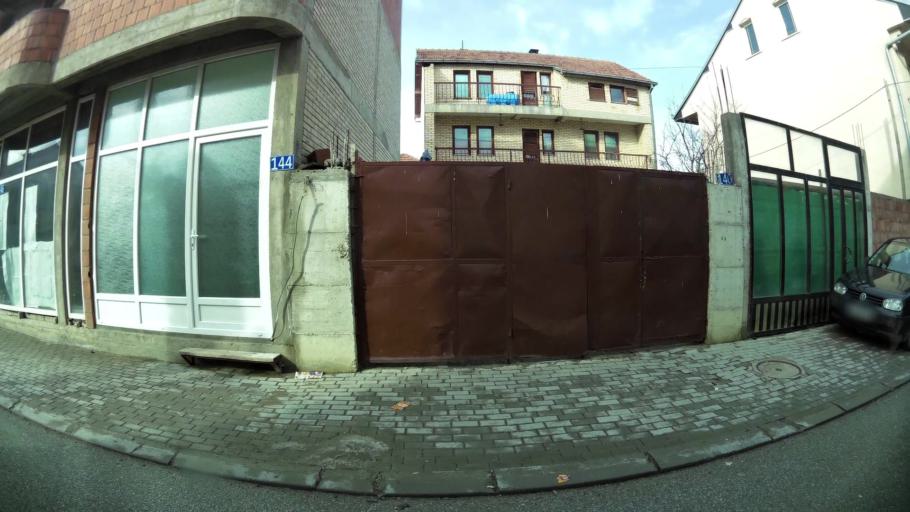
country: XK
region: Pristina
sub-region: Komuna e Prishtines
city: Pristina
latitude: 42.6764
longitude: 21.1572
